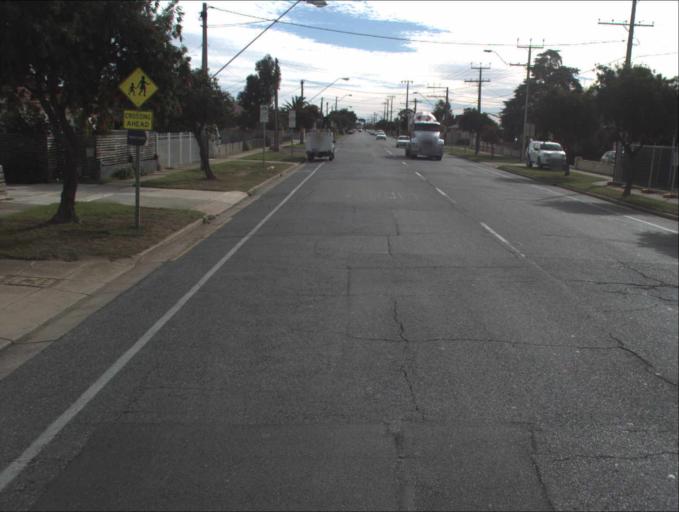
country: AU
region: South Australia
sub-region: Port Adelaide Enfield
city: Alberton
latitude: -34.8624
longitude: 138.5293
